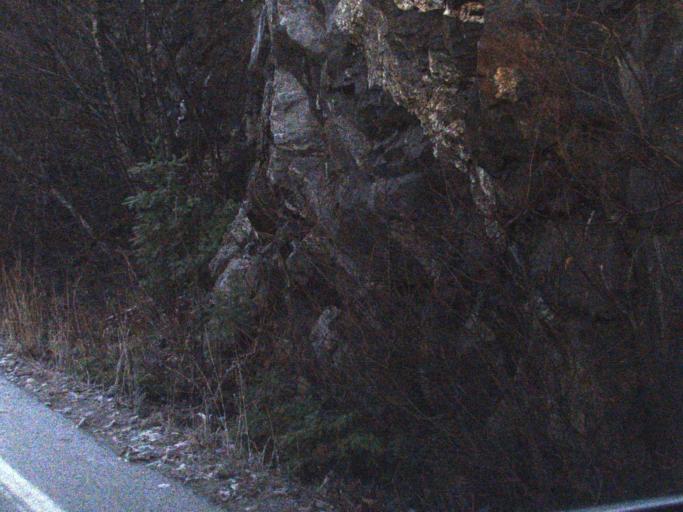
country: US
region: Washington
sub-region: Snohomish County
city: Darrington
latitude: 48.7009
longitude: -121.0965
